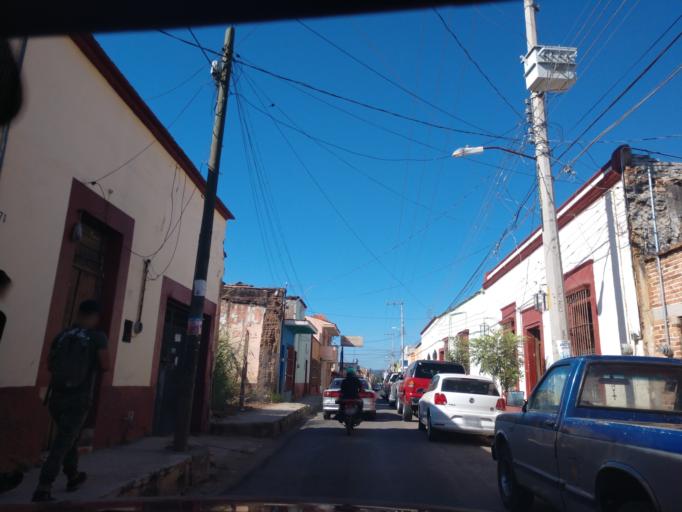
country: MX
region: Nayarit
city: Compostela
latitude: 21.2382
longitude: -104.9016
